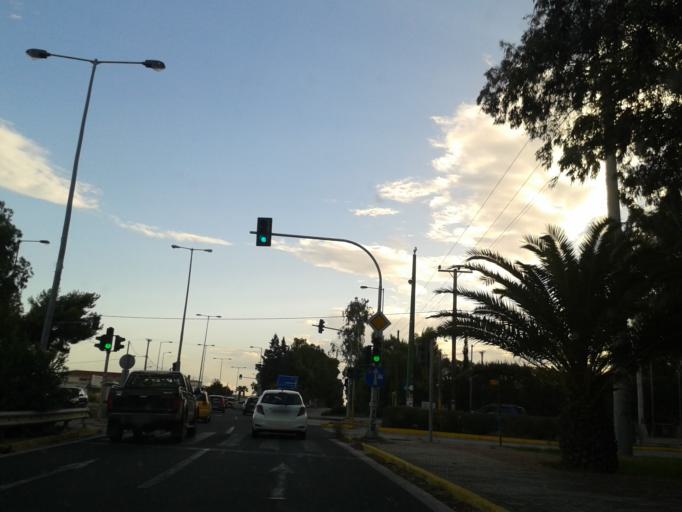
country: GR
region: Attica
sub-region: Nomarchia Anatolikis Attikis
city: Neos Voutzas
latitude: 38.0334
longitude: 23.9846
